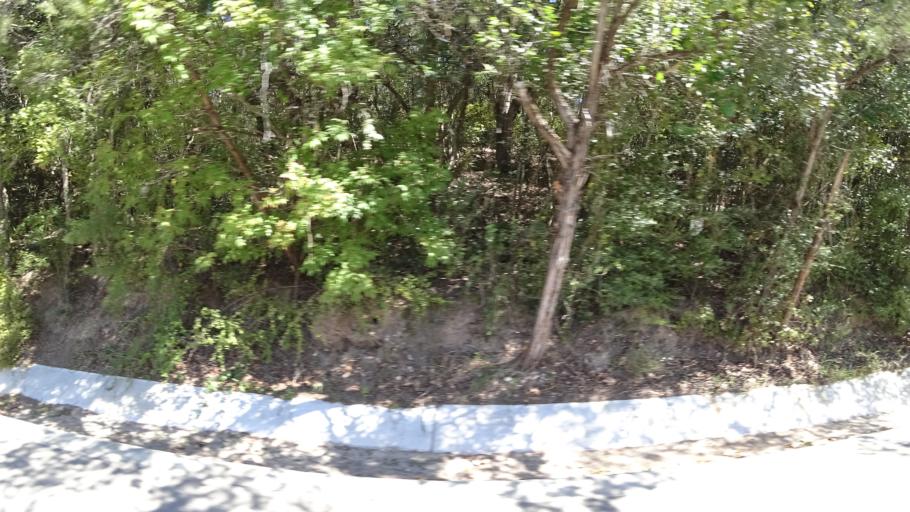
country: US
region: Texas
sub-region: Travis County
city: West Lake Hills
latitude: 30.3352
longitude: -97.7806
